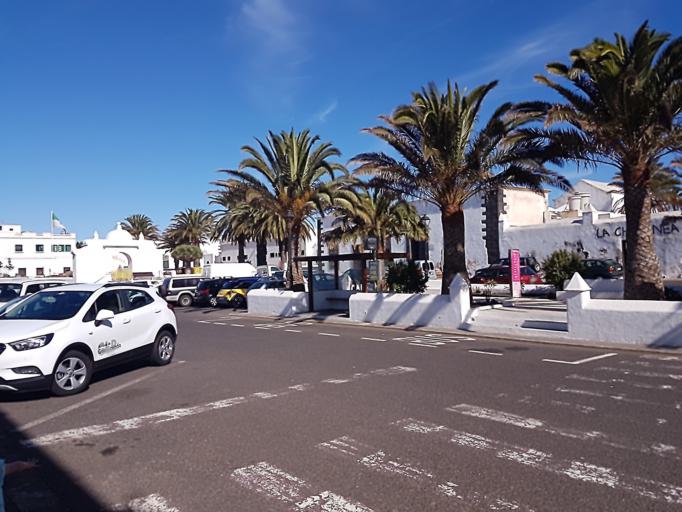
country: ES
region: Canary Islands
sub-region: Provincia de Las Palmas
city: Teguise
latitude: 29.0575
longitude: -13.5613
